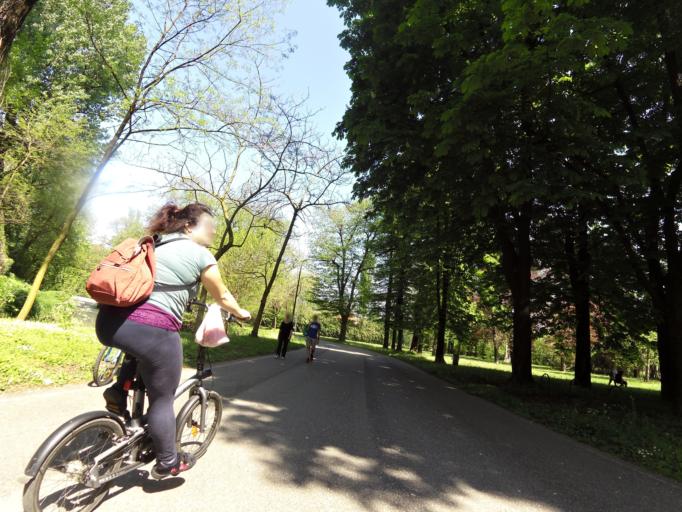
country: IT
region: Lombardy
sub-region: Citta metropolitana di Milano
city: Novegro-Tregarezzo-San Felice
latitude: 45.4941
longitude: 9.2488
